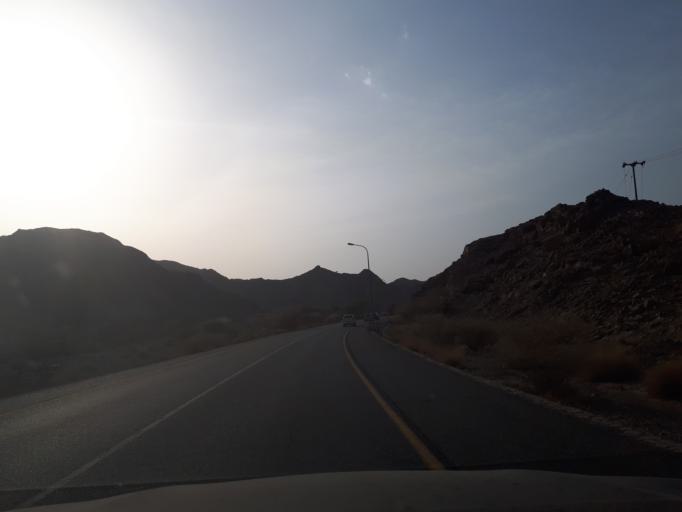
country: OM
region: Muhafazat ad Dakhiliyah
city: Sufalat Sama'il
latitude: 23.1608
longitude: 58.1065
